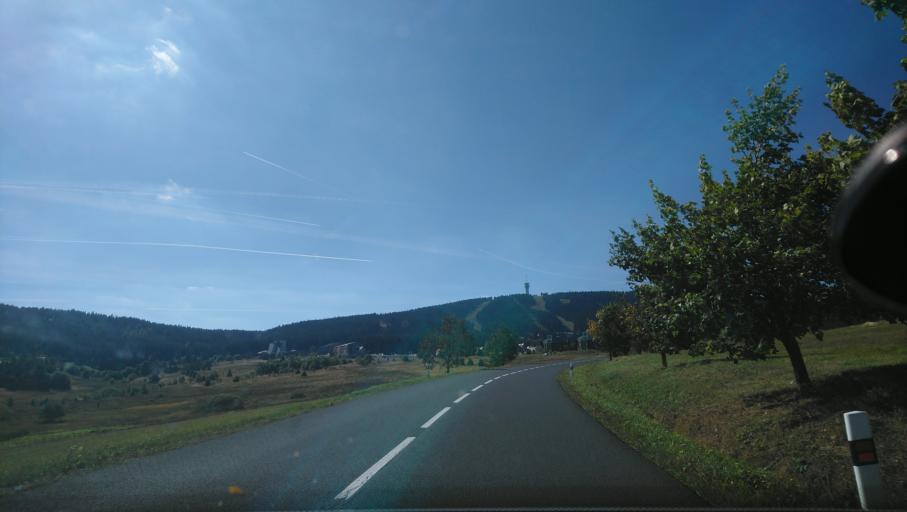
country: DE
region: Saxony
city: Kurort Oberwiesenthal
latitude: 50.4108
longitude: 12.9886
